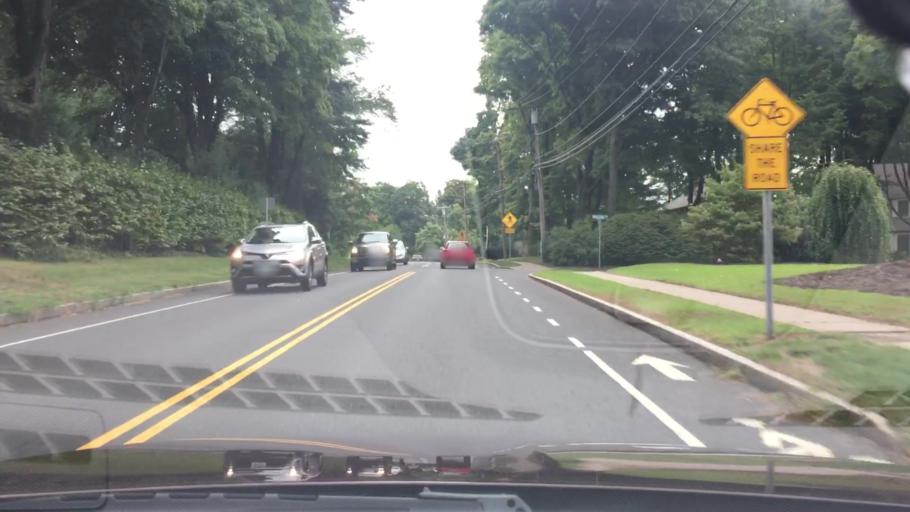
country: US
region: Connecticut
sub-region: Hartford County
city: West Hartford
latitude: 41.7607
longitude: -72.7643
